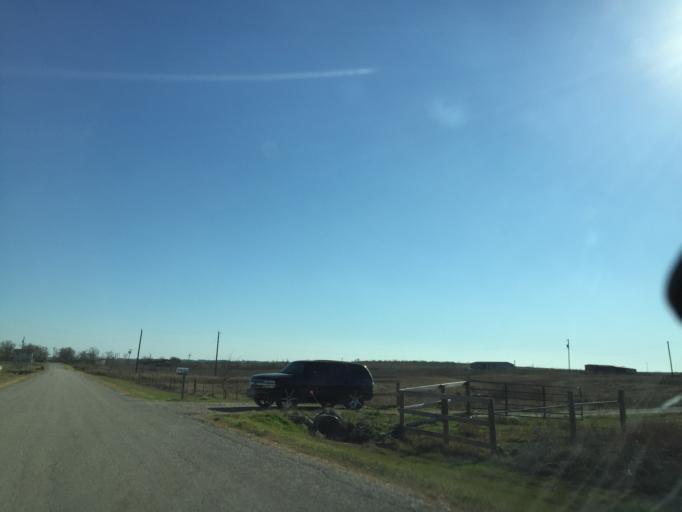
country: US
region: Texas
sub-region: Williamson County
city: Taylor
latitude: 30.5618
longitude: -97.3063
